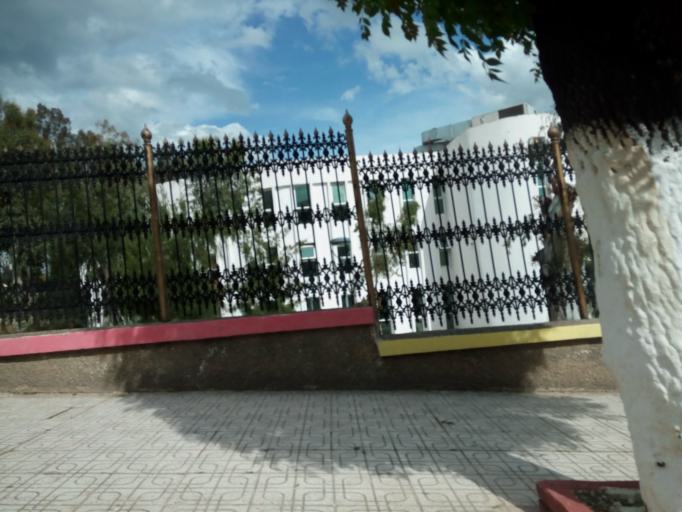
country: DZ
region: Constantine
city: Constantine
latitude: 36.3518
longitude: 6.6086
